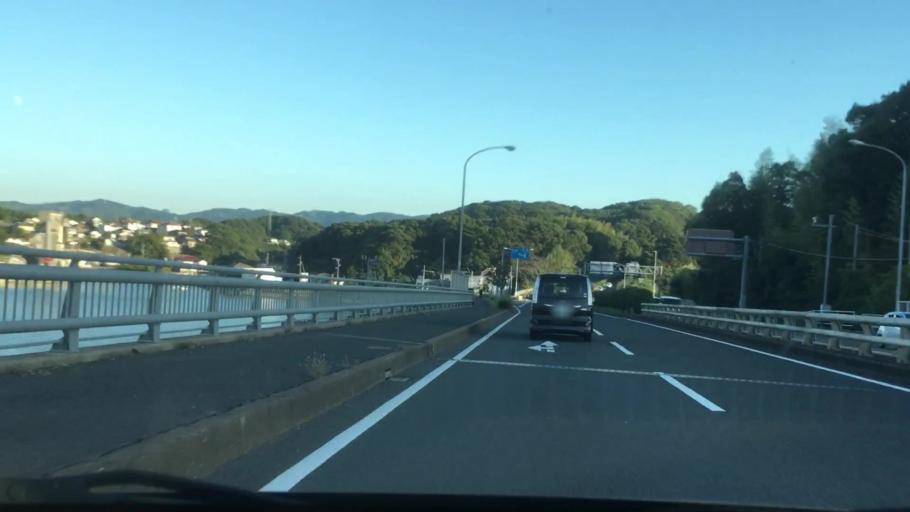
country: JP
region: Nagasaki
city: Sasebo
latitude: 33.1417
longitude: 129.7823
